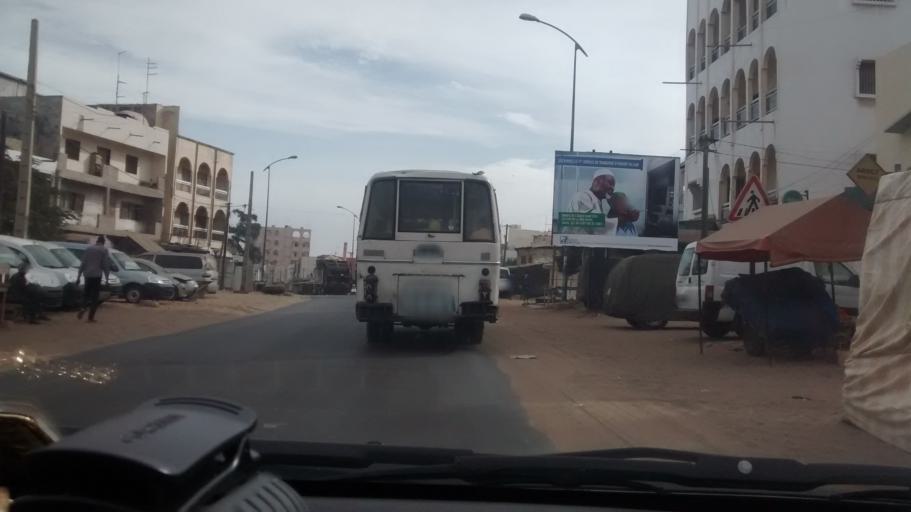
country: SN
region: Dakar
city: Pikine
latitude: 14.7655
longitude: -17.4168
